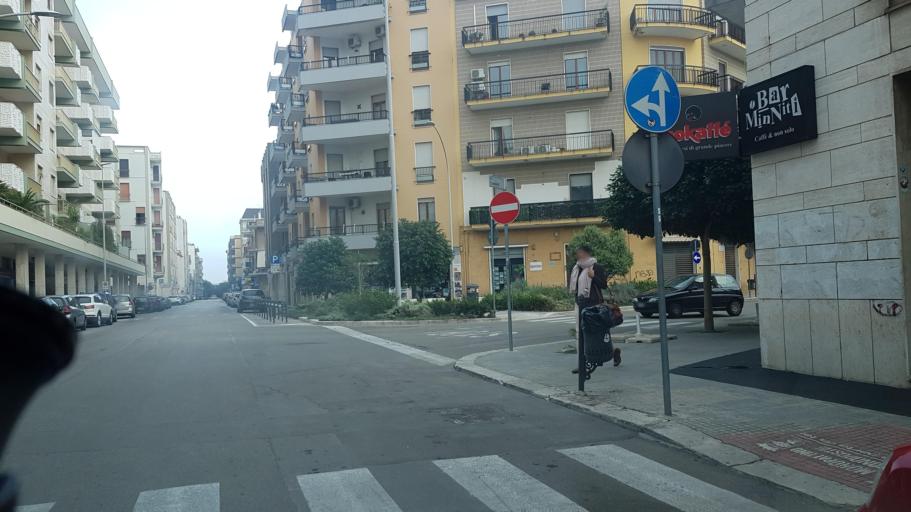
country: IT
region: Apulia
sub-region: Provincia di Lecce
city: Lecce
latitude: 40.3519
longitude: 18.1809
